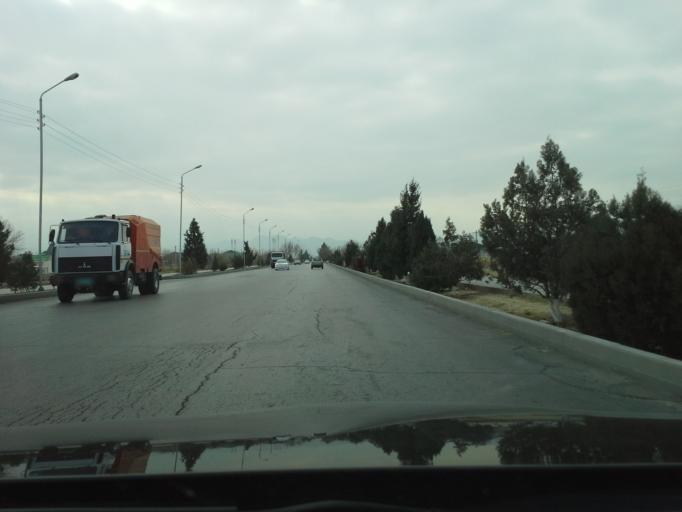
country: TM
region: Ahal
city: Abadan
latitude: 38.0341
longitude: 58.2692
